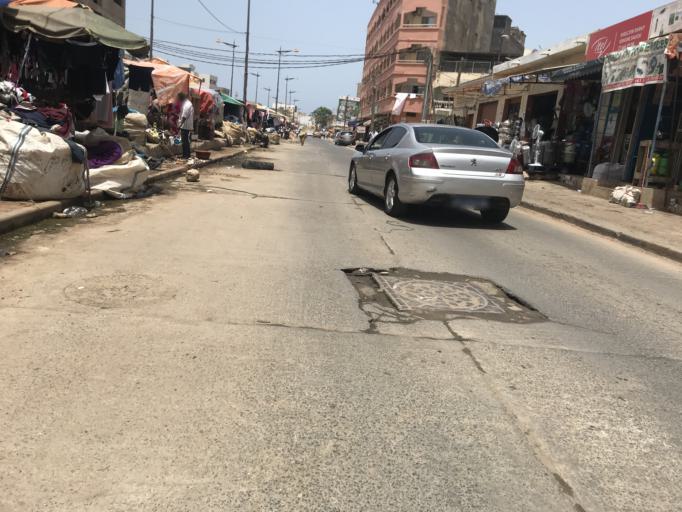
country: SN
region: Dakar
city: Dakar
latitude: 14.6823
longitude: -17.4546
